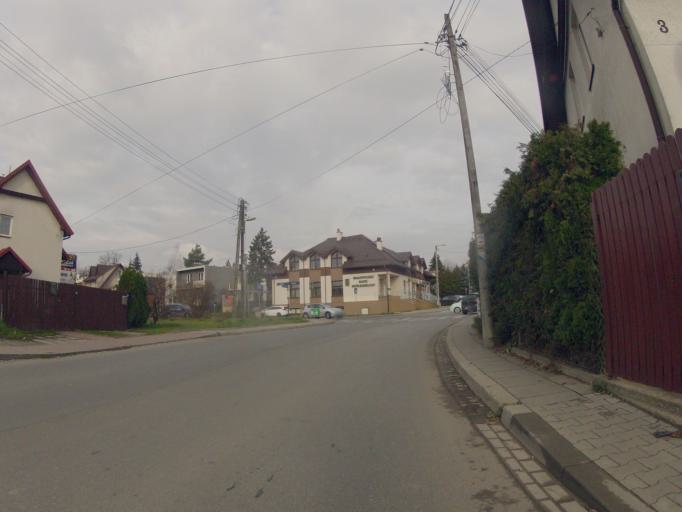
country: PL
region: Lesser Poland Voivodeship
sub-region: Powiat krakowski
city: Rzaska
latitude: 50.0830
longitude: 19.8483
